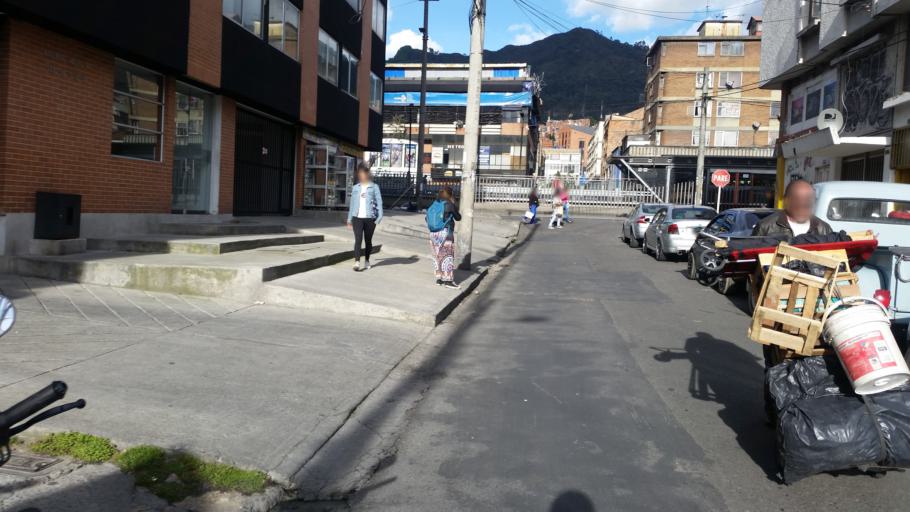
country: CO
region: Bogota D.C.
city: Bogota
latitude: 4.6434
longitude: -74.0662
